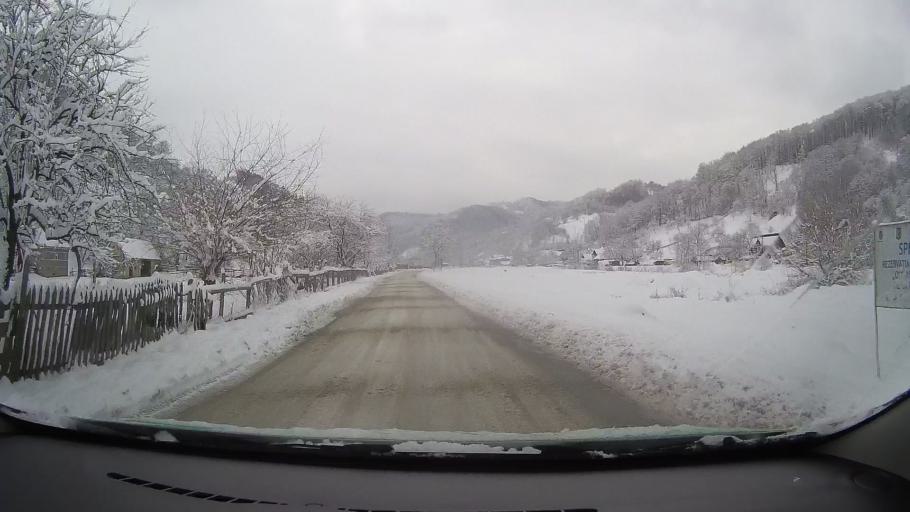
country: RO
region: Alba
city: Pianu de Sus
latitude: 45.8610
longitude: 23.4986
